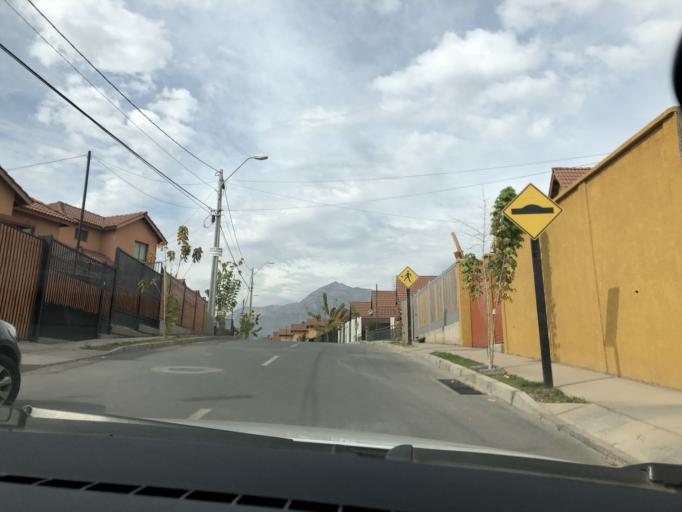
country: CL
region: Santiago Metropolitan
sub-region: Provincia de Cordillera
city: Puente Alto
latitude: -33.5869
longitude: -70.5319
